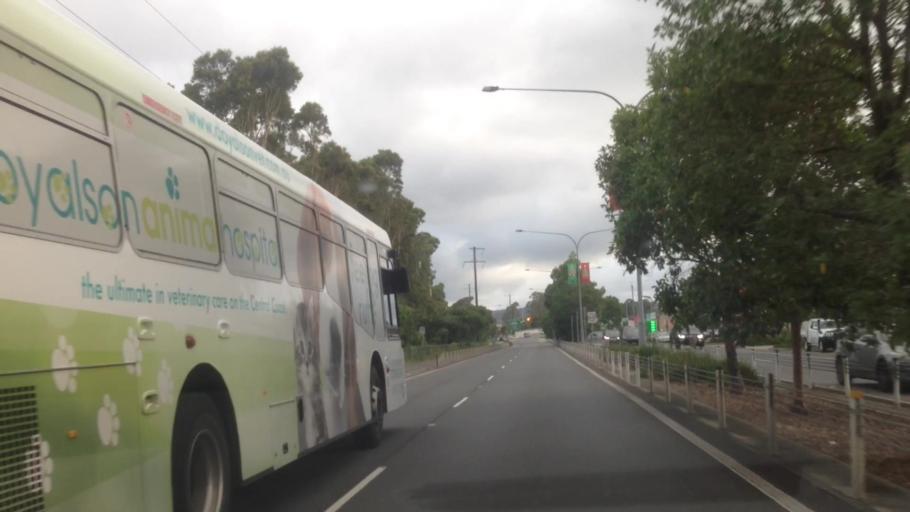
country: AU
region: New South Wales
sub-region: Wyong Shire
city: Chittaway Bay
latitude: -33.3043
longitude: 151.4205
